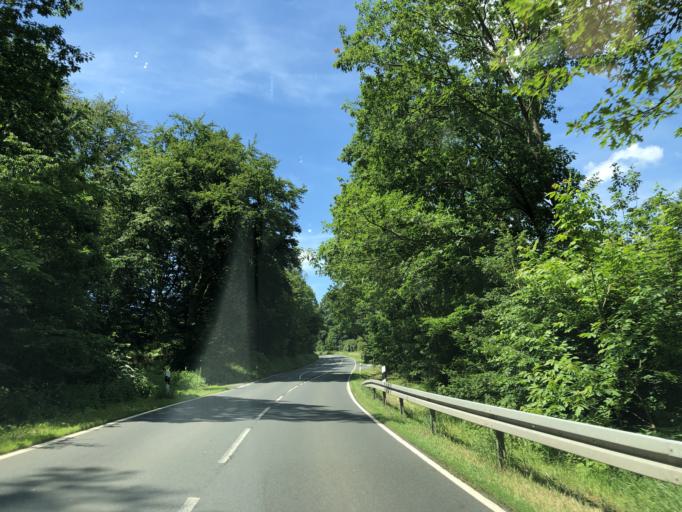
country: DE
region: Hesse
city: Wetter
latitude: 50.8456
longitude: 8.6744
